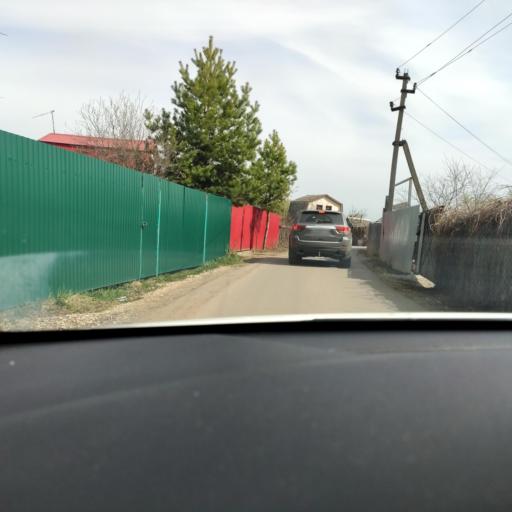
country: RU
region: Tatarstan
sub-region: Gorod Kazan'
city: Kazan
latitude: 55.8515
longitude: 49.1662
